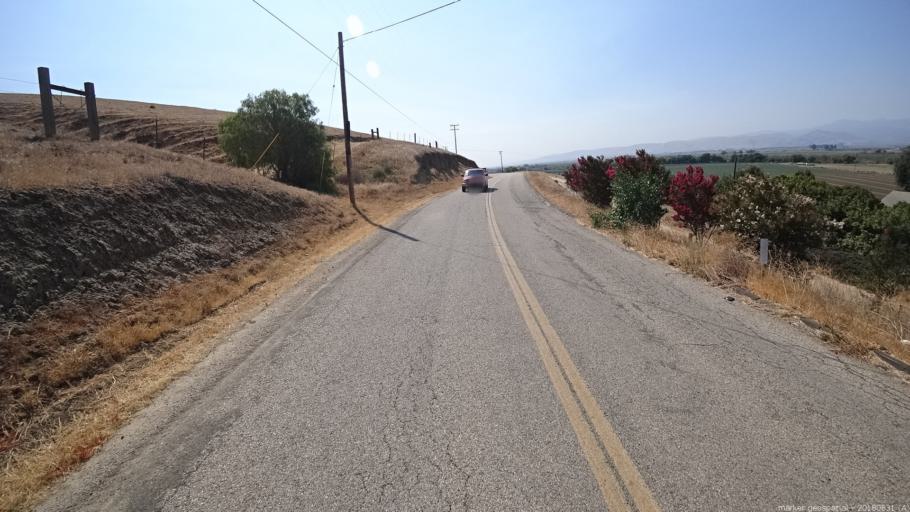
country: US
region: California
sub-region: Monterey County
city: Greenfield
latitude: 36.3836
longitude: -121.2447
